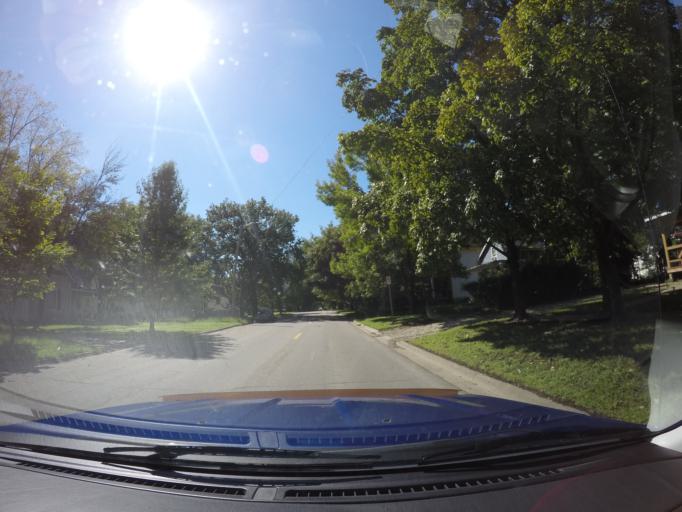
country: US
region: Kansas
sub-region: Douglas County
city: Lawrence
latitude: 38.9627
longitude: -95.2324
